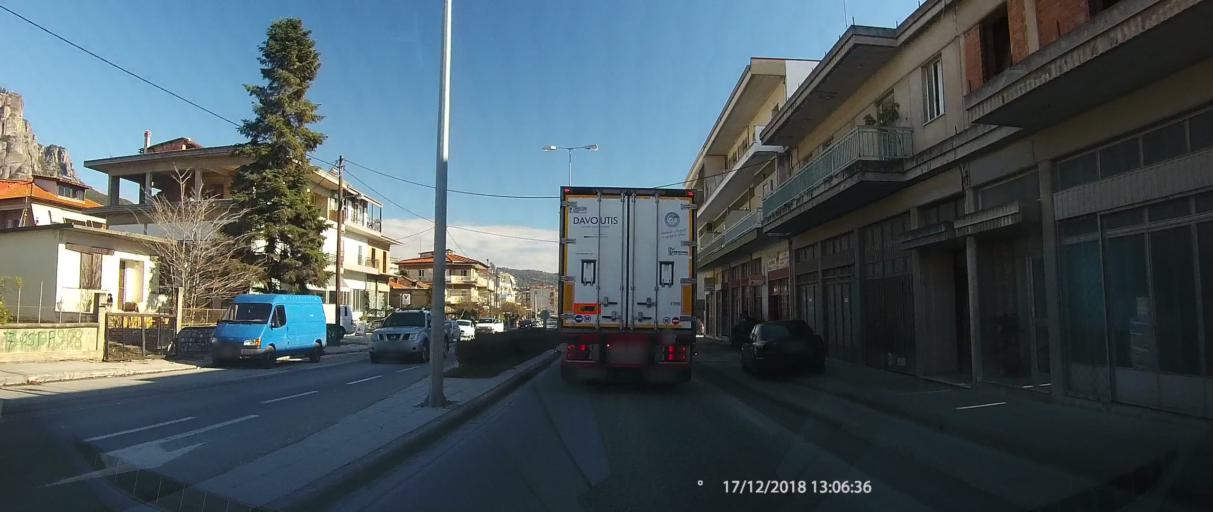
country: GR
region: Thessaly
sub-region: Trikala
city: Kalampaka
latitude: 39.7023
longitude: 21.6280
